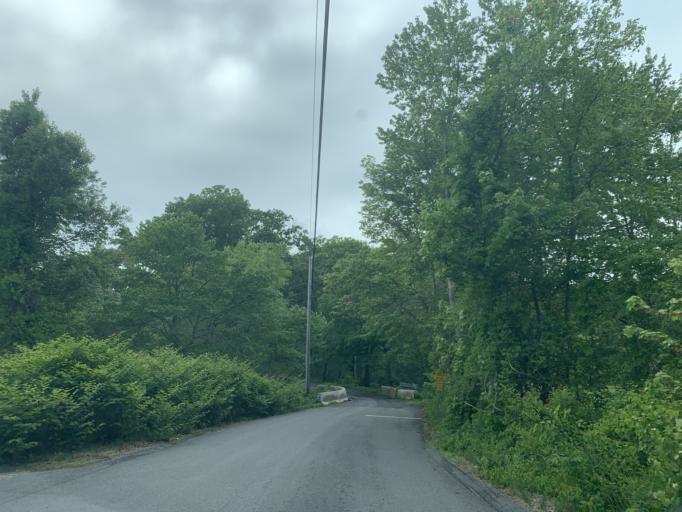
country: US
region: Massachusetts
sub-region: Worcester County
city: Grafton
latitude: 42.2022
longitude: -71.6517
